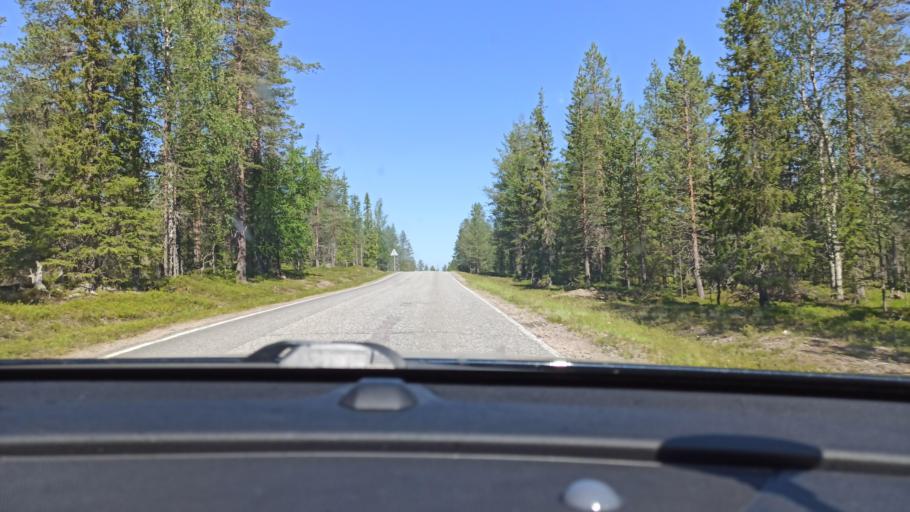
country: FI
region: Lapland
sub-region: Tunturi-Lappi
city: Kolari
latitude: 67.6796
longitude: 24.1394
